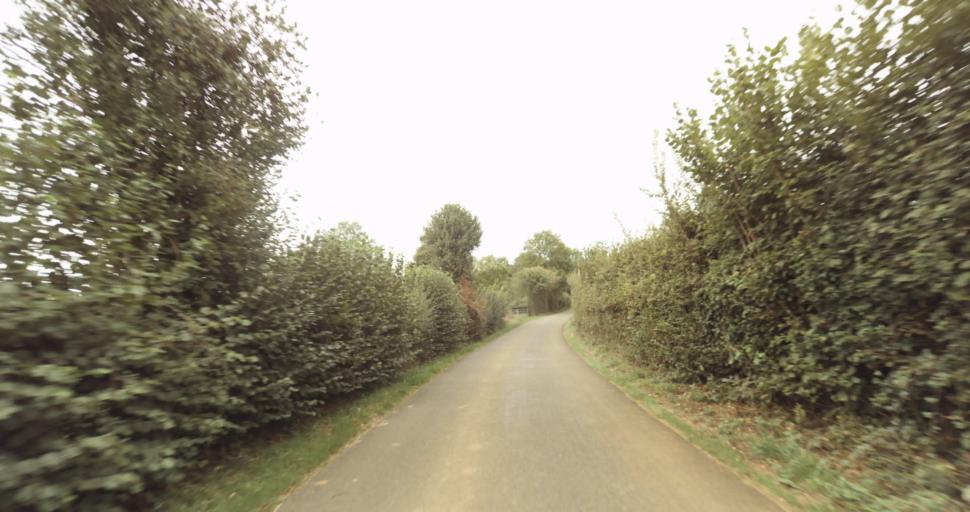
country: FR
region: Lower Normandy
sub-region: Departement de l'Orne
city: Gace
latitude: 48.7209
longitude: 0.3208
